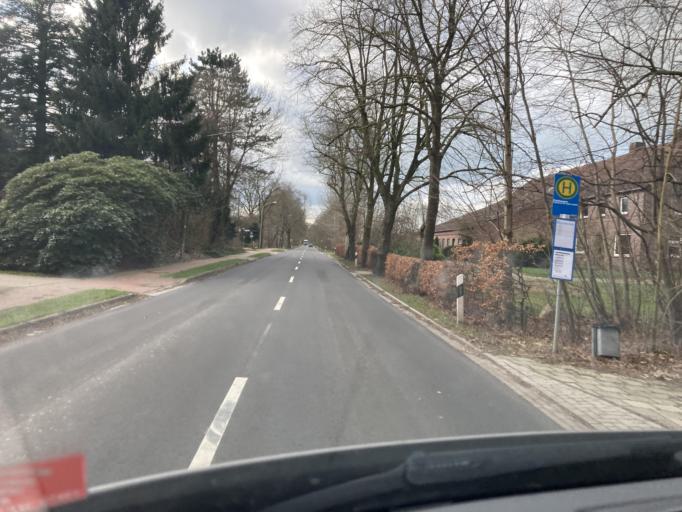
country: DE
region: Lower Saxony
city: Filsum
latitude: 53.1866
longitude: 7.6117
